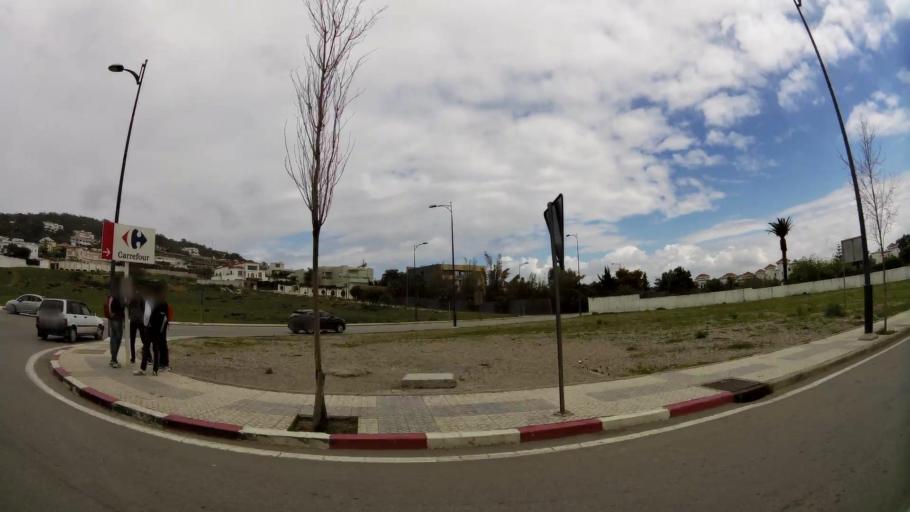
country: MA
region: Tanger-Tetouan
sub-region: Tanger-Assilah
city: Boukhalef
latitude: 35.7759
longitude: -5.8590
